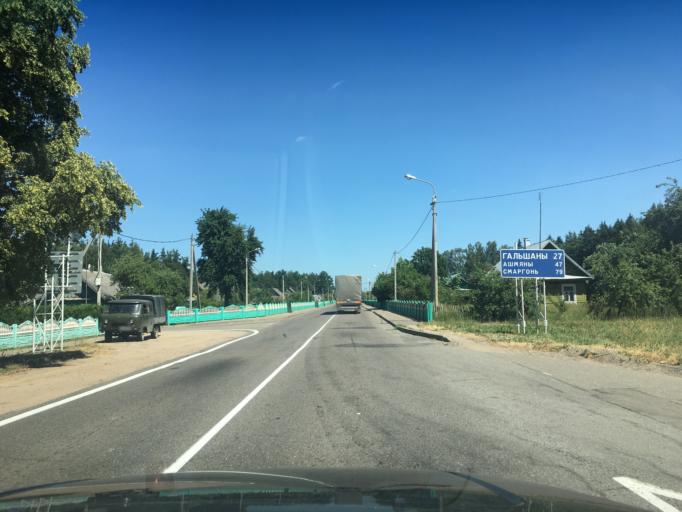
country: BY
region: Grodnenskaya
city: Iwye
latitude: 54.0260
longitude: 25.9203
